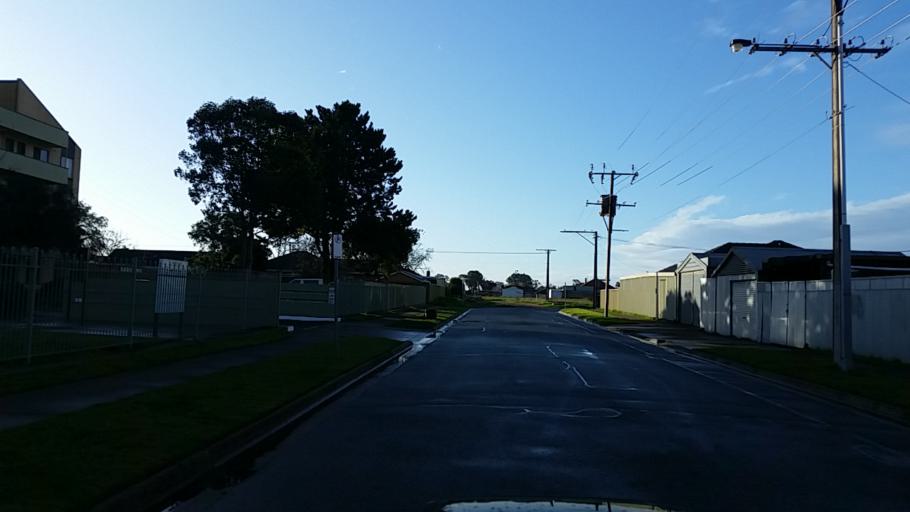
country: AU
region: South Australia
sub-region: Charles Sturt
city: Findon
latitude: -34.9041
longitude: 138.5348
